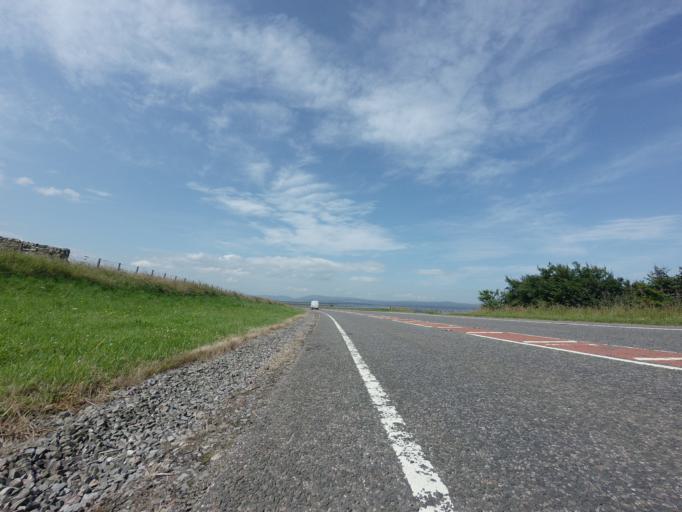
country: GB
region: Scotland
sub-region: Highland
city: Tain
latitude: 57.8285
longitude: -4.0830
